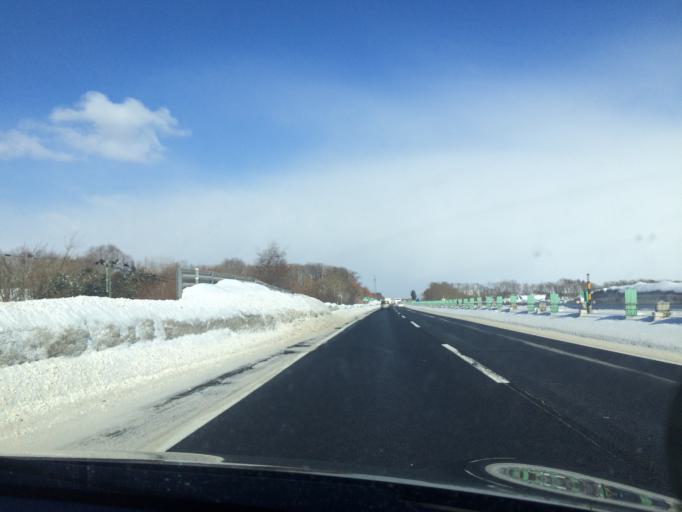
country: JP
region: Hokkaido
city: Kitahiroshima
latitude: 42.8924
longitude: 141.5492
